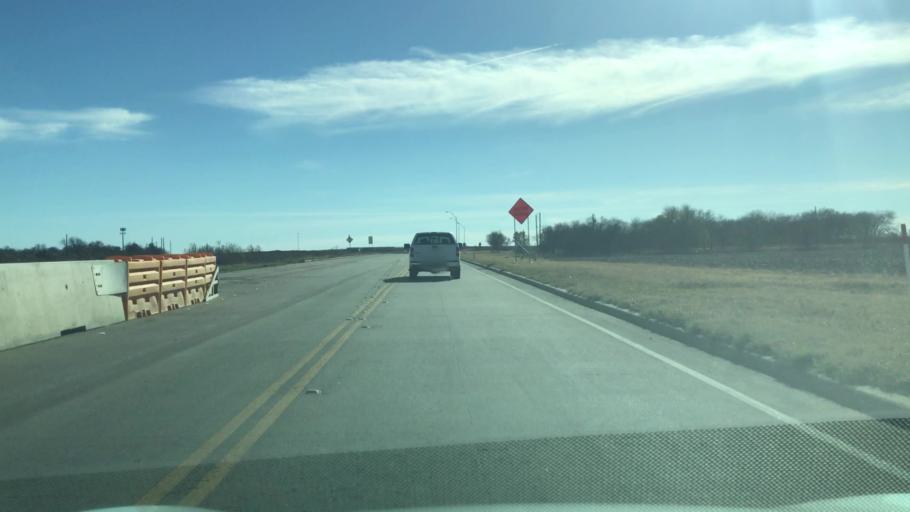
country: US
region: Texas
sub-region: Tarrant County
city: Mansfield
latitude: 32.5324
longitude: -97.0824
